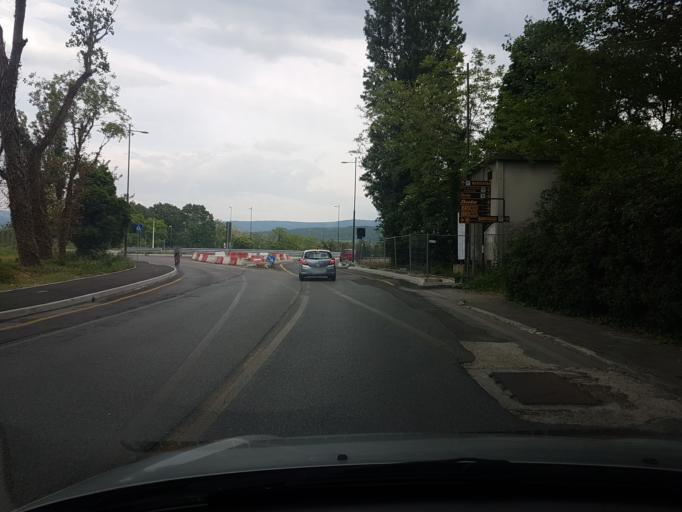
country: IT
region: Friuli Venezia Giulia
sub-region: Provincia di Trieste
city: Muggia
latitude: 45.5976
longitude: 13.7839
